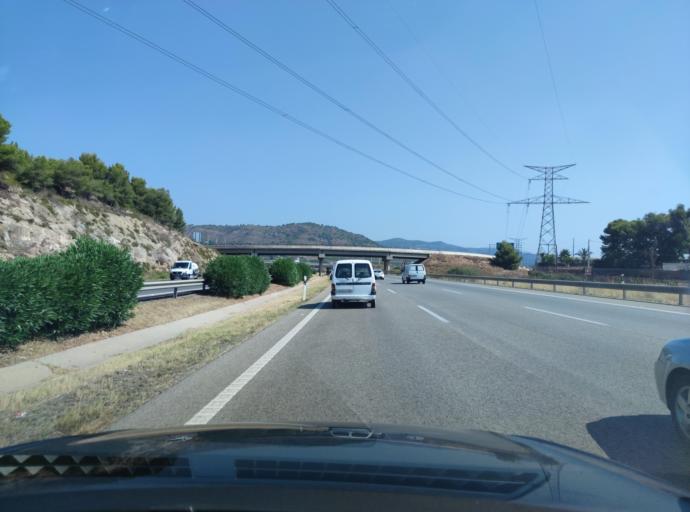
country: ES
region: Valencia
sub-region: Provincia de Valencia
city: Petres
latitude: 39.6695
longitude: -0.3014
